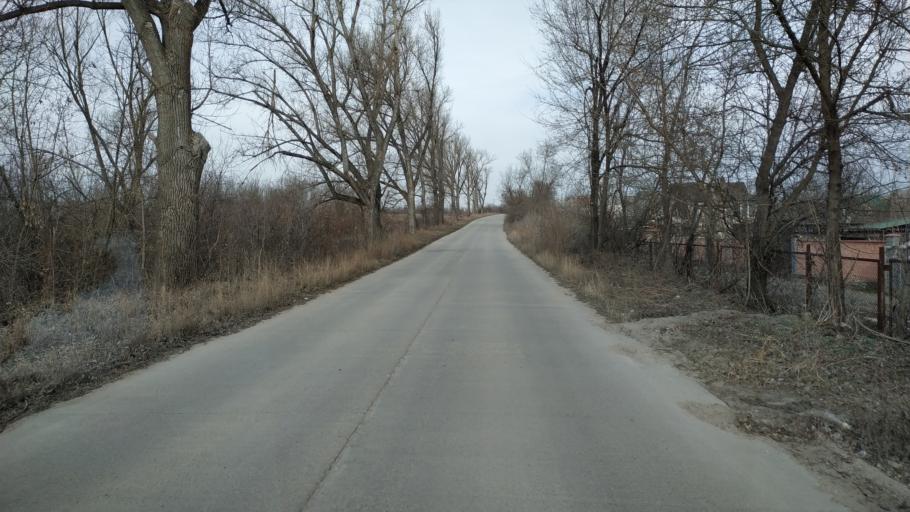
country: MD
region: Chisinau
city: Vatra
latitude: 47.0940
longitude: 28.7370
